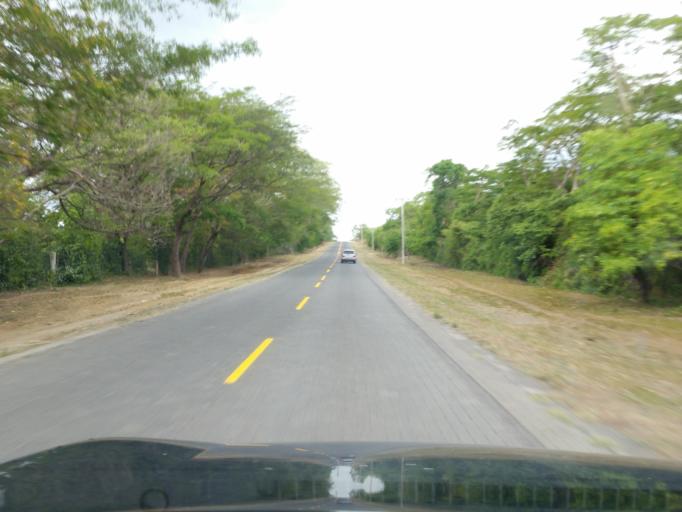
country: NI
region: Managua
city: San Rafael del Sur
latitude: 11.8894
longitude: -86.5141
